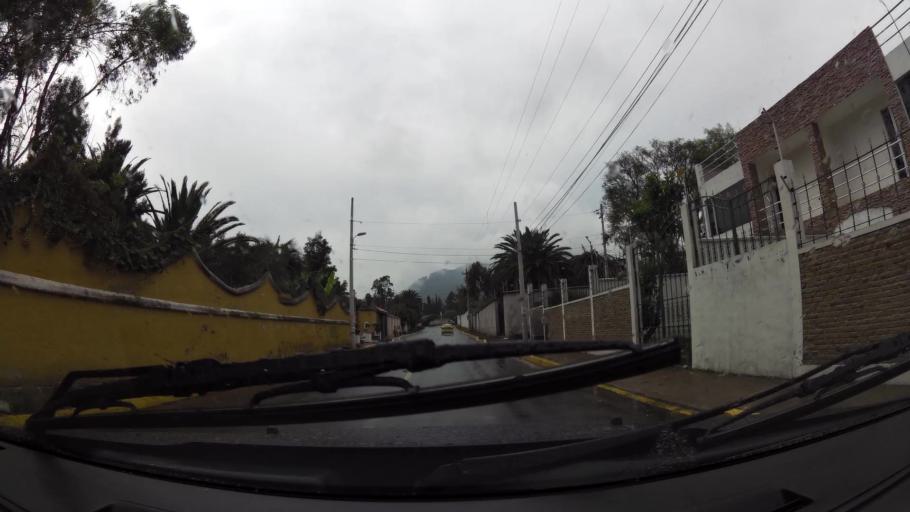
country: EC
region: Pichincha
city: Sangolqui
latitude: -0.2878
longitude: -78.4573
